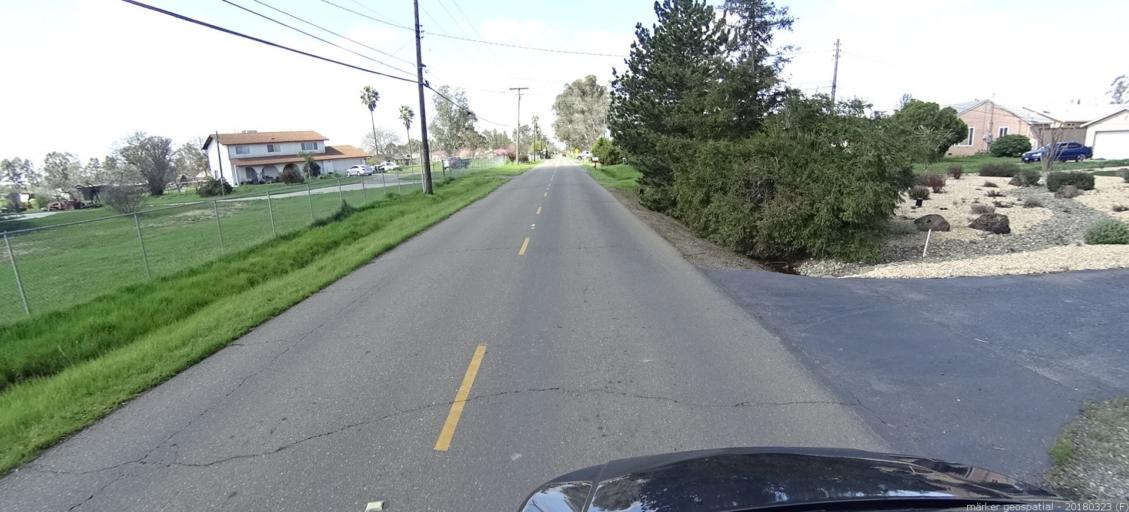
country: US
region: California
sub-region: Sacramento County
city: Rio Linda
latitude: 38.6836
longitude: -121.4223
